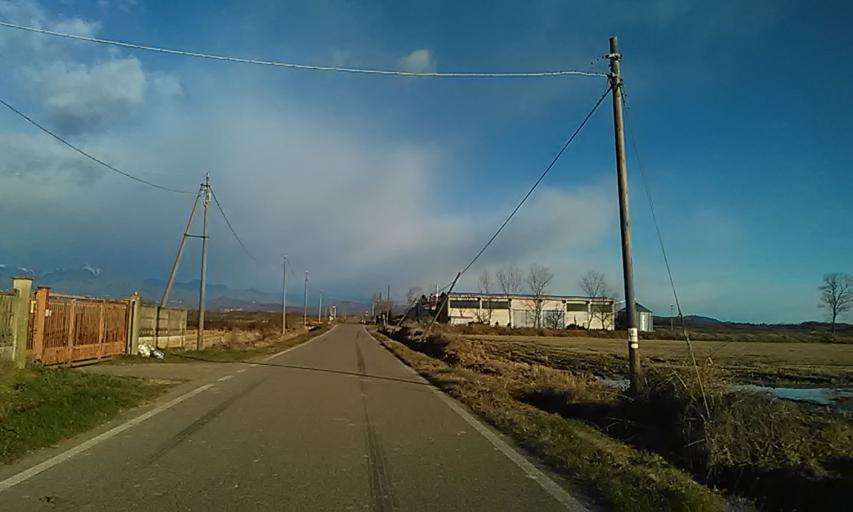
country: IT
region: Piedmont
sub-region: Provincia di Vercelli
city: Buronzo
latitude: 45.5042
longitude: 8.2700
